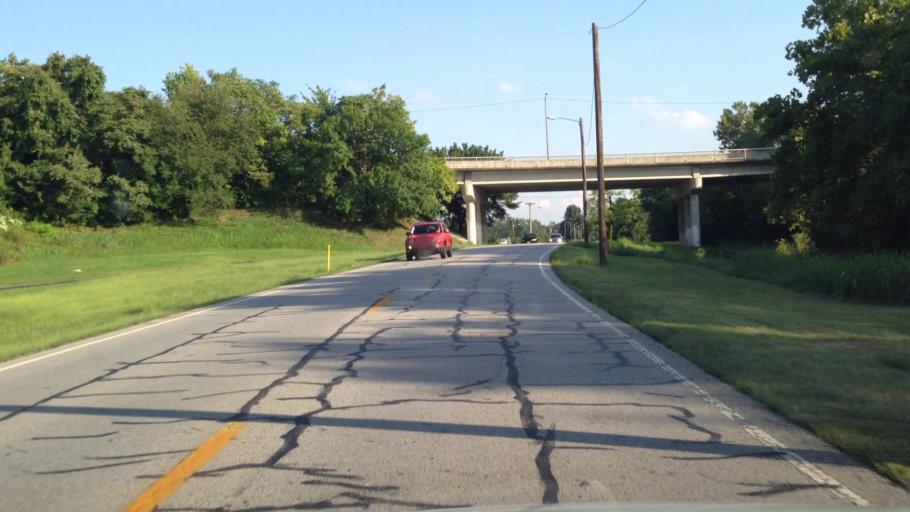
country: US
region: Missouri
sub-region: Jasper County
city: Joplin
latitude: 37.0921
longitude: -94.5097
